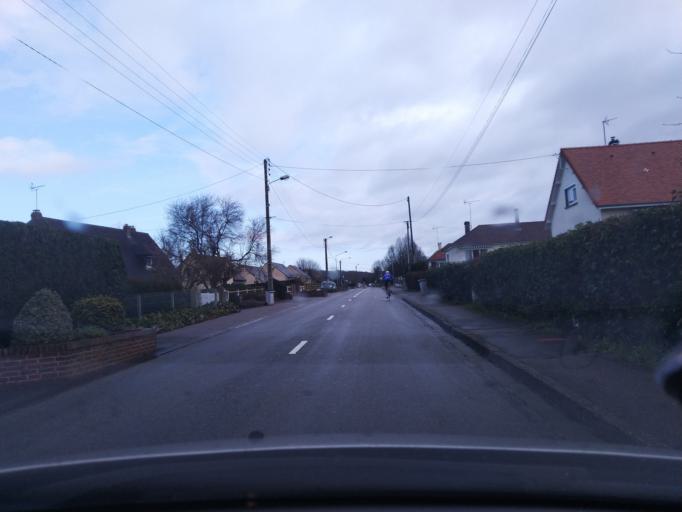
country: FR
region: Haute-Normandie
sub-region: Departement de la Seine-Maritime
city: Duclair
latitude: 49.4884
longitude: 0.8808
